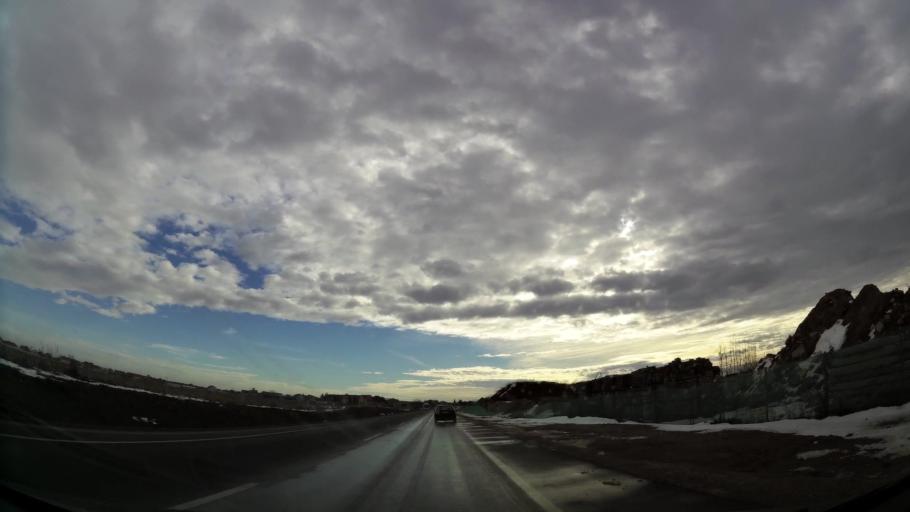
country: RS
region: Central Serbia
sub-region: Belgrade
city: Surcin
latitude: 44.8031
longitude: 20.3135
